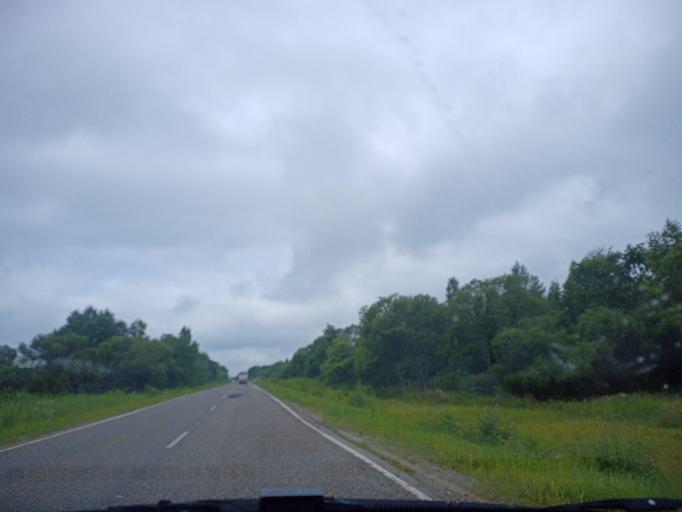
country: RU
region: Primorskiy
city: Novopokrovka
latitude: 45.9705
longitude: 134.2381
